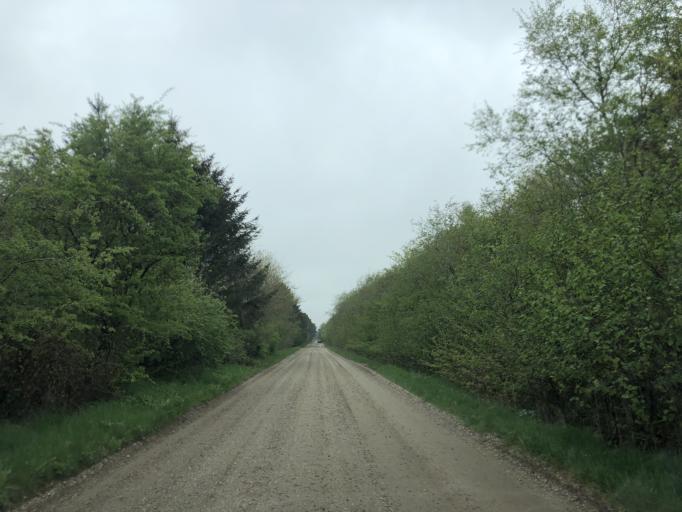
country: DK
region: Central Jutland
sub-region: Lemvig Kommune
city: Lemvig
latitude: 56.5090
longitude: 8.3190
